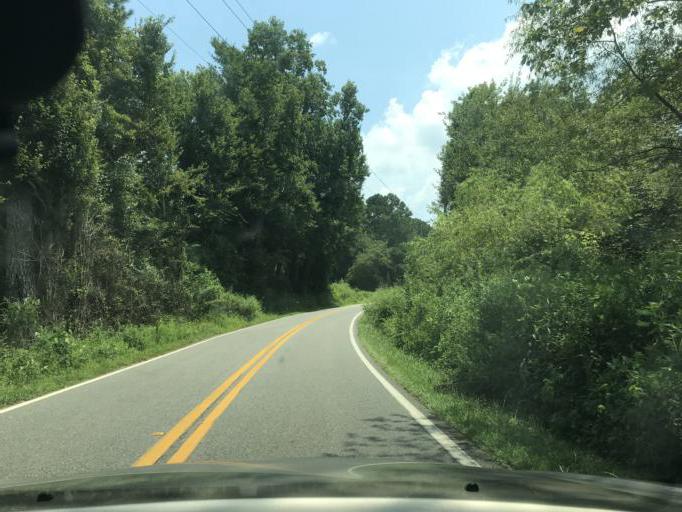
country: US
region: Georgia
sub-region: Forsyth County
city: Cumming
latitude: 34.2640
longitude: -84.1541
